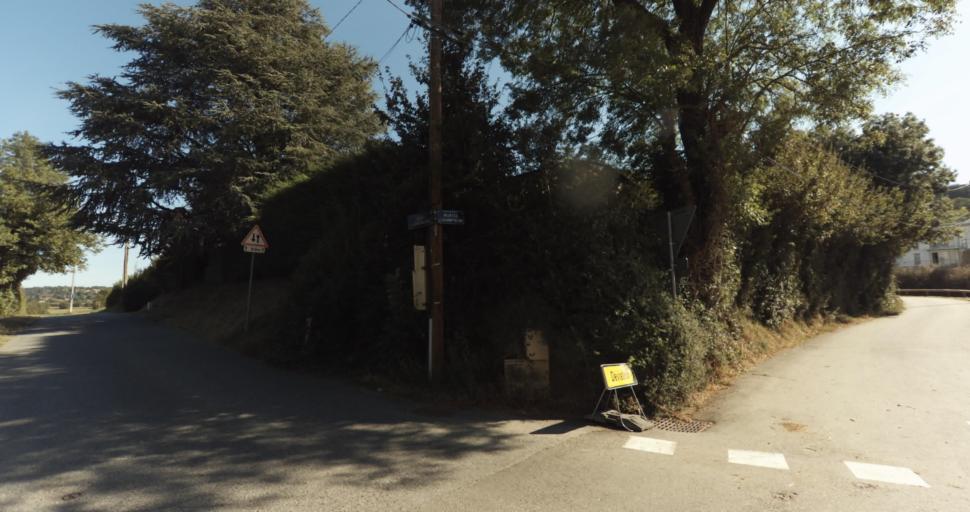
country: FR
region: Rhone-Alpes
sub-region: Departement du Rhone
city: Fleurieu-sur-Saone
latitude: 45.8657
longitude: 4.8503
